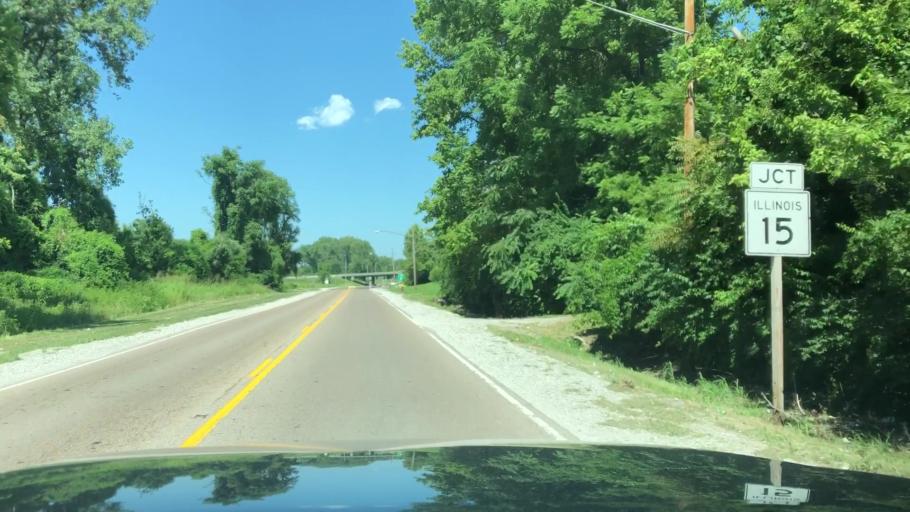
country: US
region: Illinois
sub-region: Saint Clair County
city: Centreville
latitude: 38.5645
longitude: -90.0944
